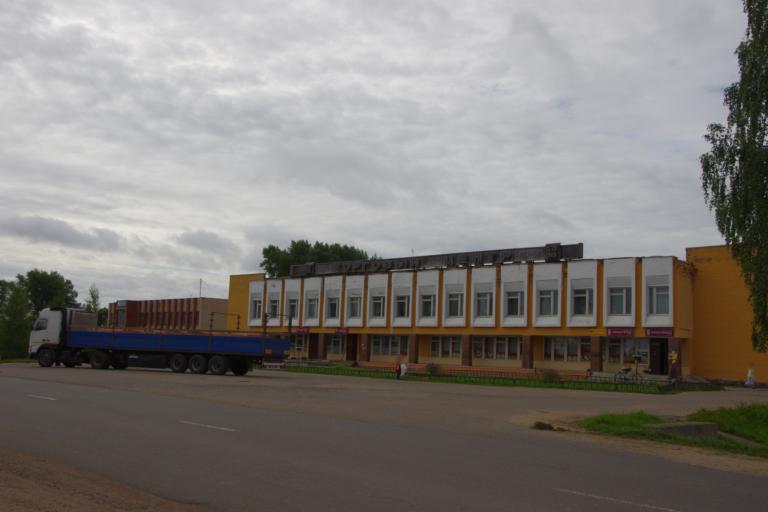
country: BY
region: Vitebsk
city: Chashniki
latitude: 55.3501
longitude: 29.3016
